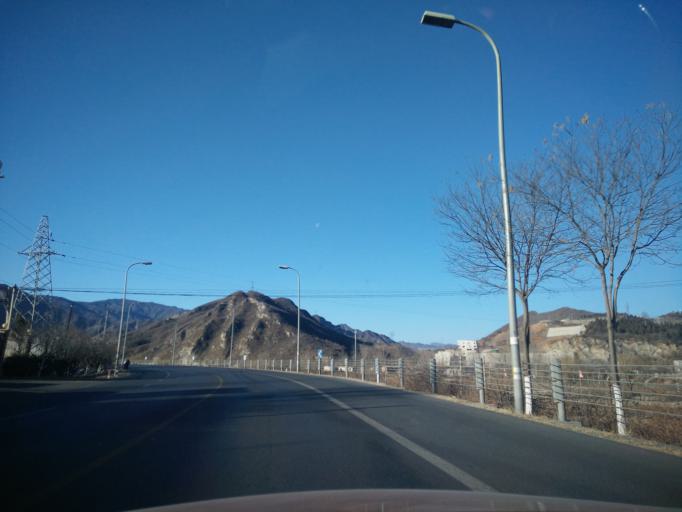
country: CN
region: Beijing
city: Miaofengshan
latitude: 39.9871
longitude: 116.0622
